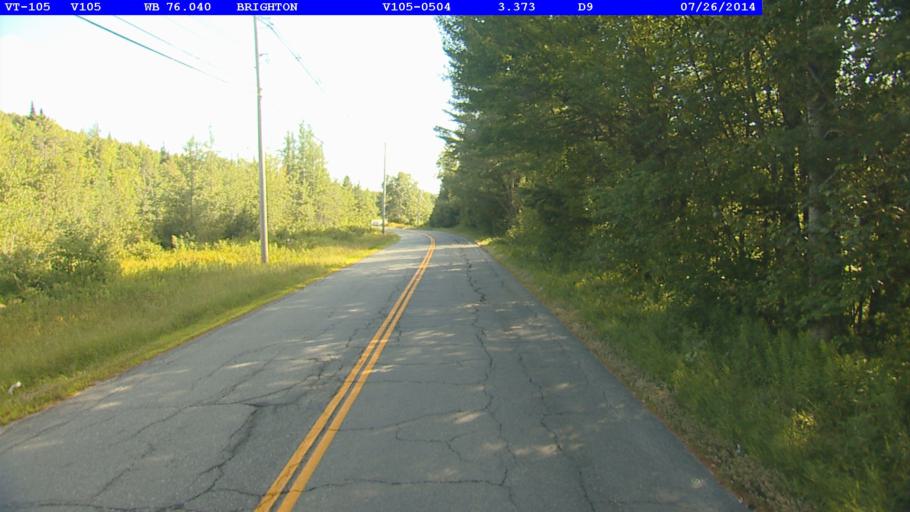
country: US
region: Vermont
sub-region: Caledonia County
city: Lyndonville
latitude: 44.8043
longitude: -71.8909
